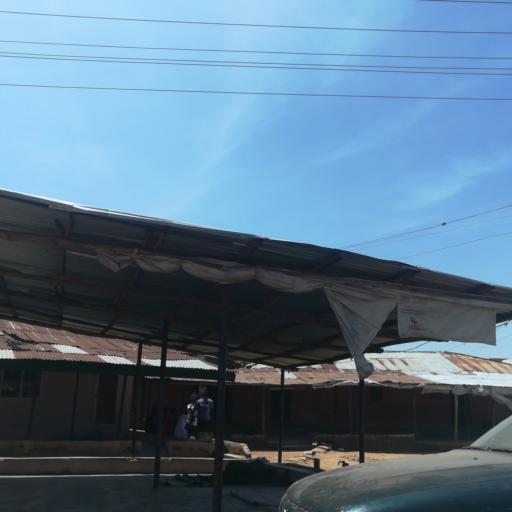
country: NG
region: Plateau
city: Bukuru
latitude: 9.7992
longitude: 8.8616
